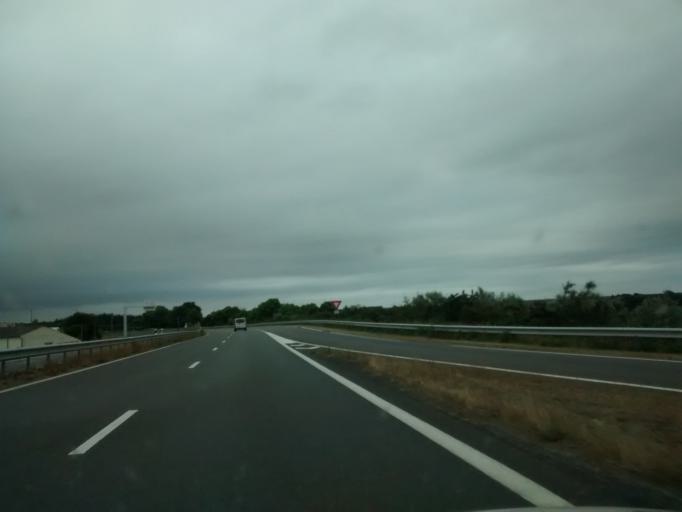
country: FR
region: Brittany
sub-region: Departement des Cotes-d'Armor
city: Rospez
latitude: 48.7055
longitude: -3.3793
